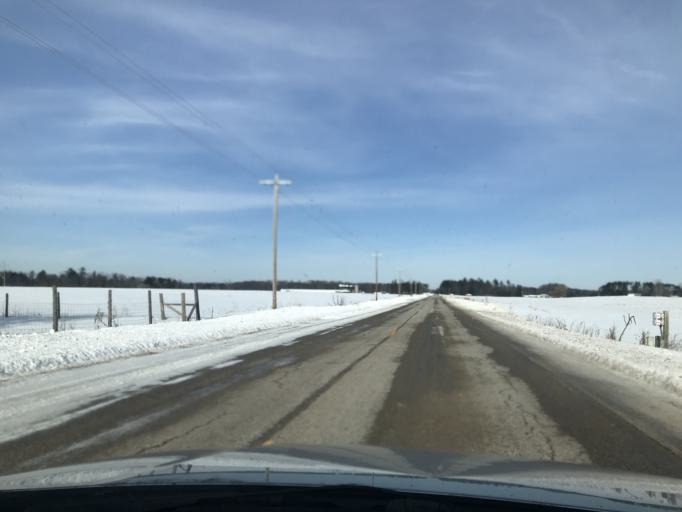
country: US
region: Wisconsin
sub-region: Oconto County
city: Oconto Falls
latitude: 45.1269
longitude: -88.1780
